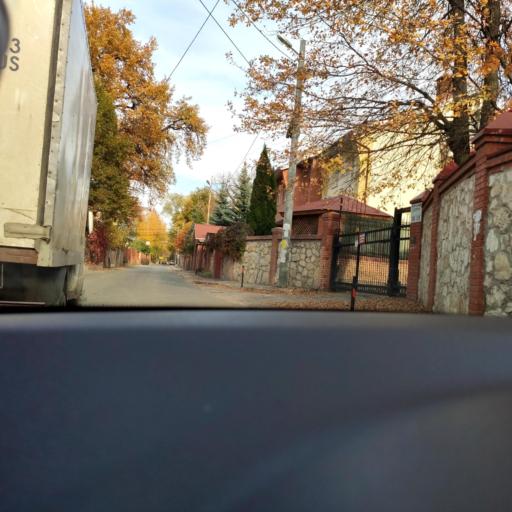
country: RU
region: Samara
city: Samara
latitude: 53.2728
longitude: 50.1932
